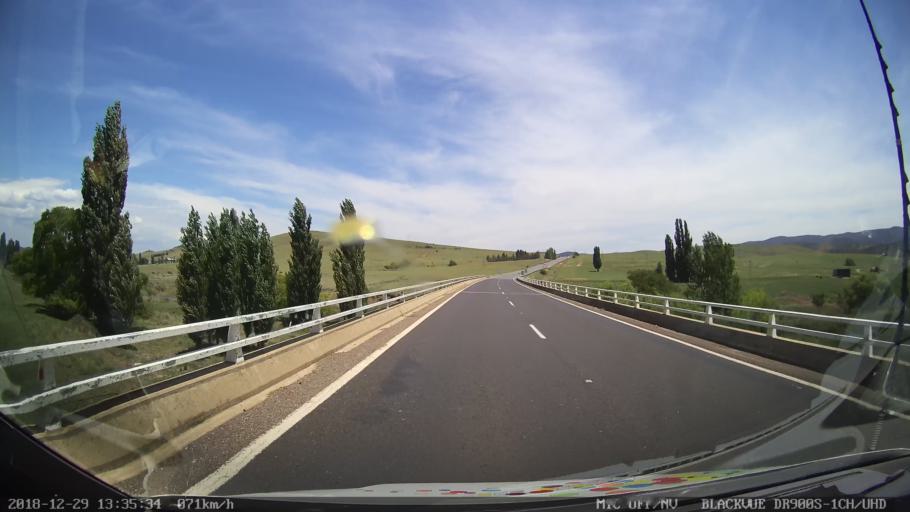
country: AU
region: New South Wales
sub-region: Cooma-Monaro
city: Cooma
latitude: -35.9607
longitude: 149.1487
